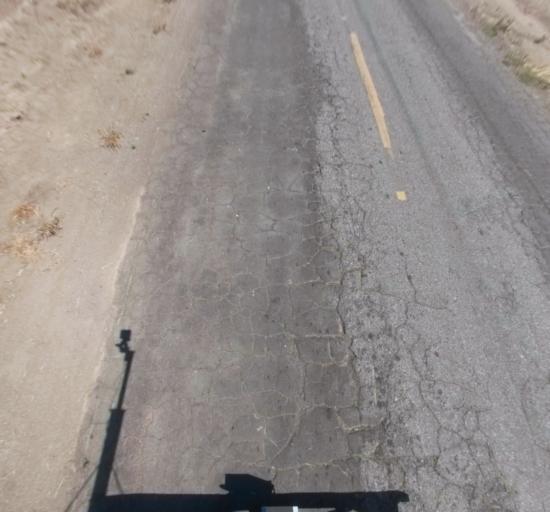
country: US
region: California
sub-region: Madera County
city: Chowchilla
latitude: 37.0656
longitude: -120.3469
